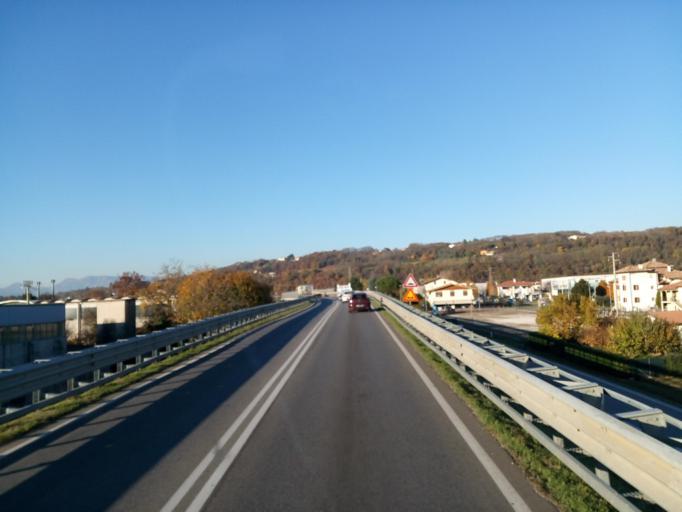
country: IT
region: Veneto
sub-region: Provincia di Treviso
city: Montebelluna
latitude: 45.7786
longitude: 12.0679
